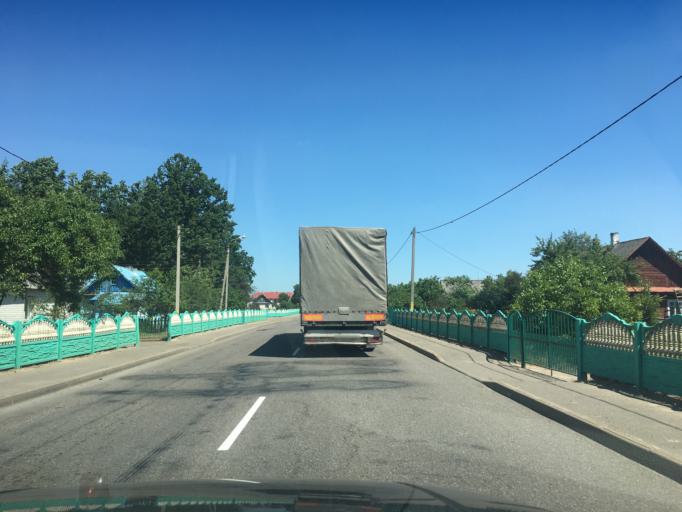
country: BY
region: Grodnenskaya
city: Iwye
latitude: 54.0284
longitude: 25.9243
